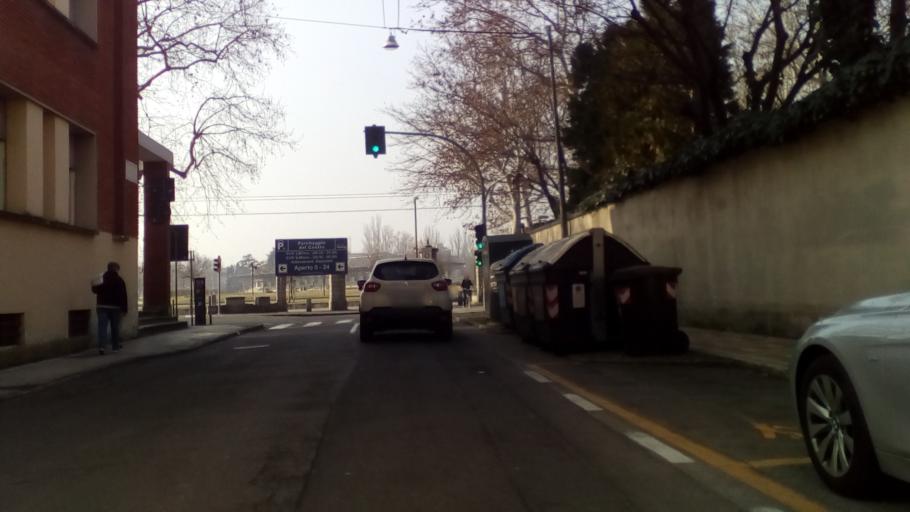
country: IT
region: Emilia-Romagna
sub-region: Provincia di Modena
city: Modena
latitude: 44.6509
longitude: 10.9258
